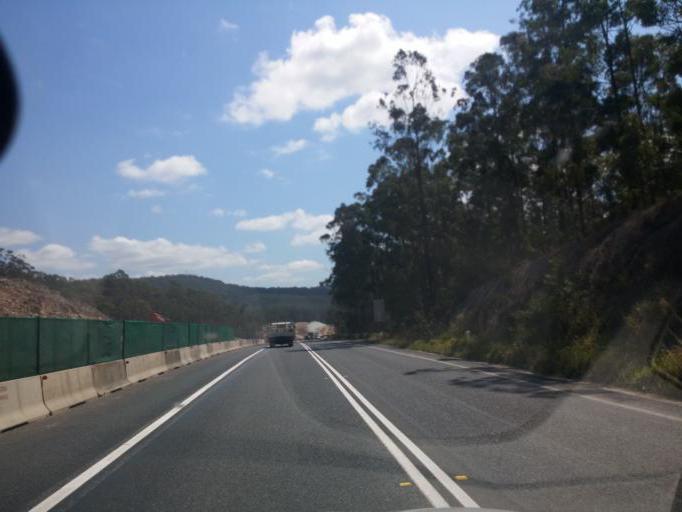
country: AU
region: New South Wales
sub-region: Port Macquarie-Hastings
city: North Shore
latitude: -31.2809
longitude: 152.8138
